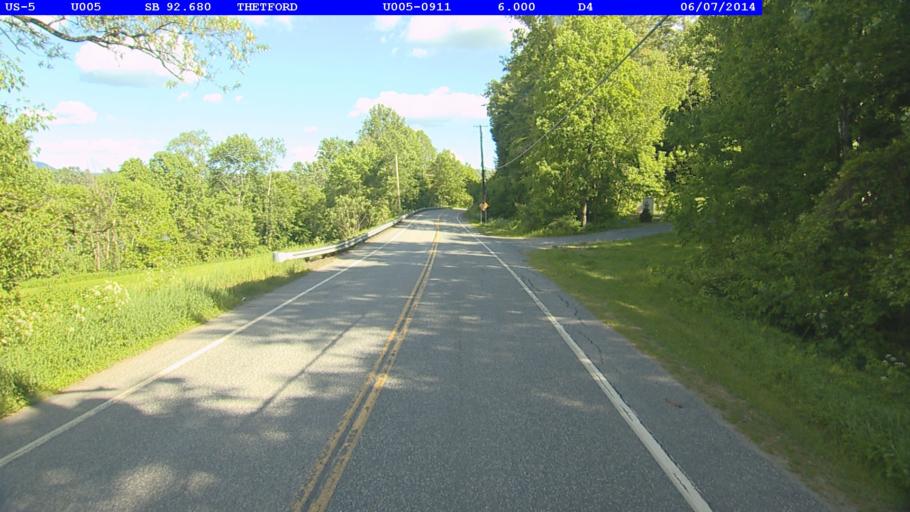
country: US
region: New Hampshire
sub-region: Grafton County
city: Lyme
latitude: 43.8521
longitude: -72.1882
